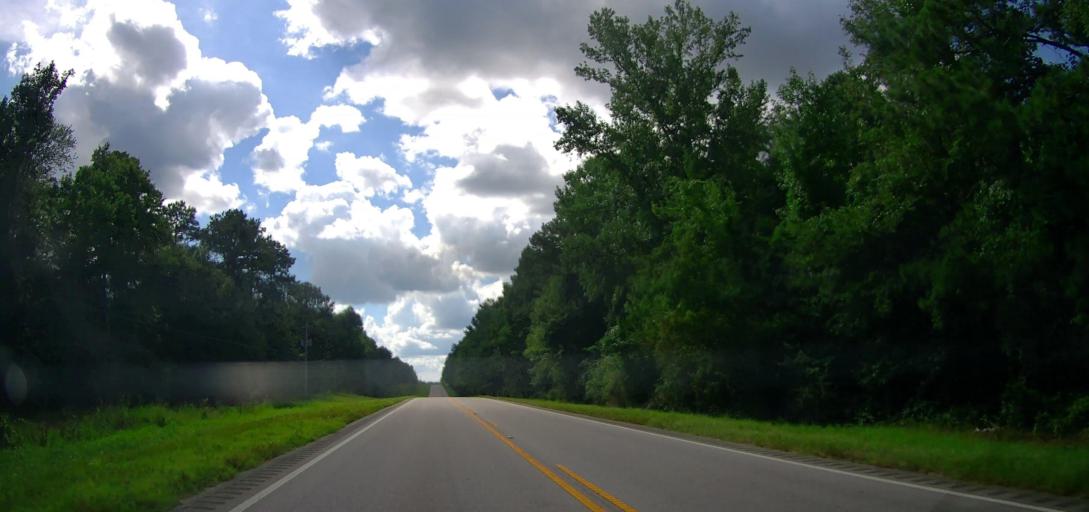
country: US
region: Alabama
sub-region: Lee County
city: Auburn
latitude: 32.4425
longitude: -85.4978
